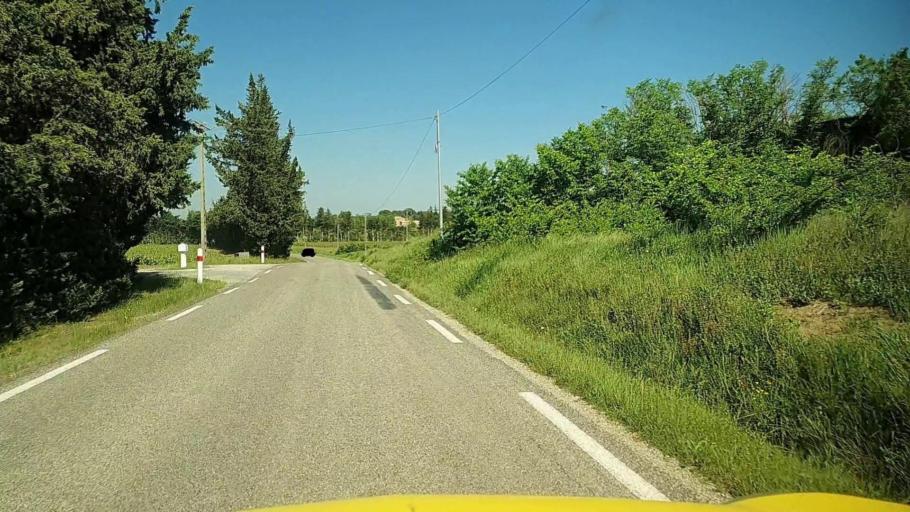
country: FR
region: Languedoc-Roussillon
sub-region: Departement du Gard
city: Saint-Chaptes
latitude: 43.9523
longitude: 4.3043
